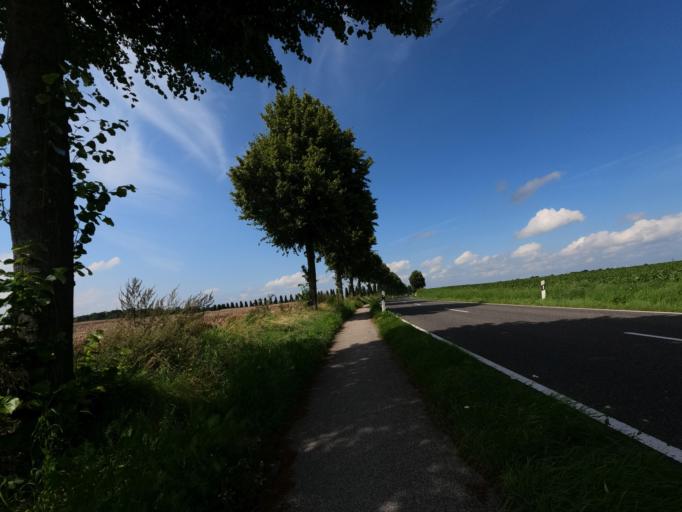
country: DE
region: North Rhine-Westphalia
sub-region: Regierungsbezirk Koln
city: Ubach-Palenberg
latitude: 50.9467
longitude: 6.1462
